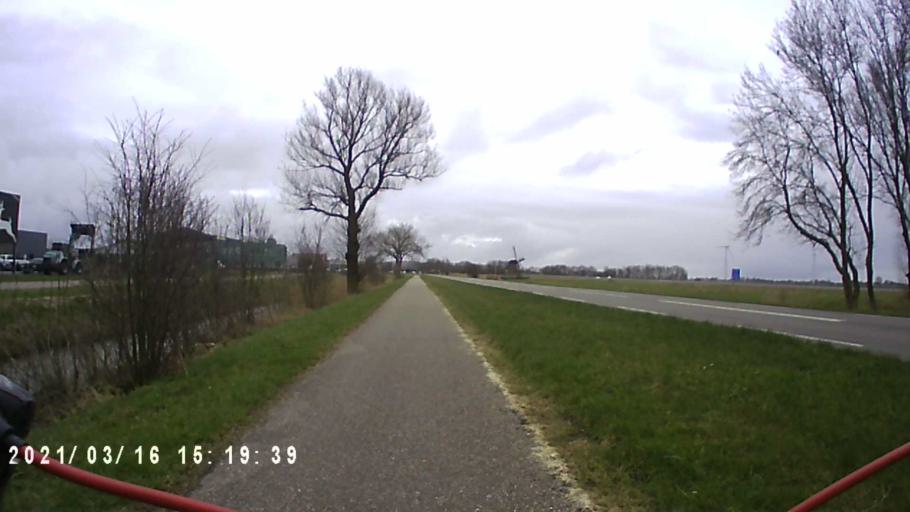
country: NL
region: Friesland
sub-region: Sudwest Fryslan
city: Bolsward
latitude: 53.0669
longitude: 5.4980
